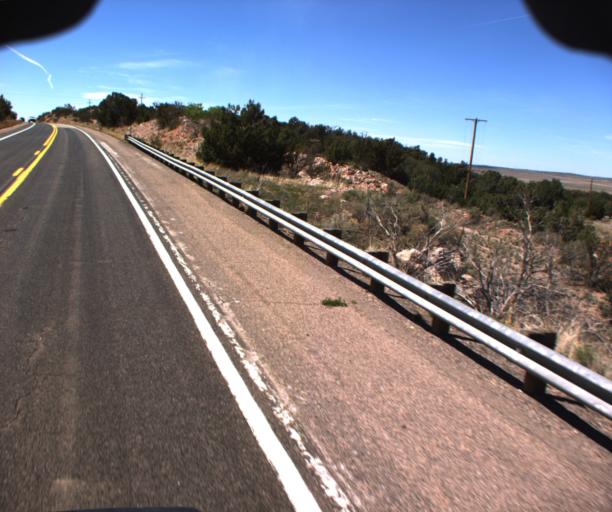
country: US
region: Arizona
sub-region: Mohave County
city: Peach Springs
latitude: 35.5255
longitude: -113.2149
